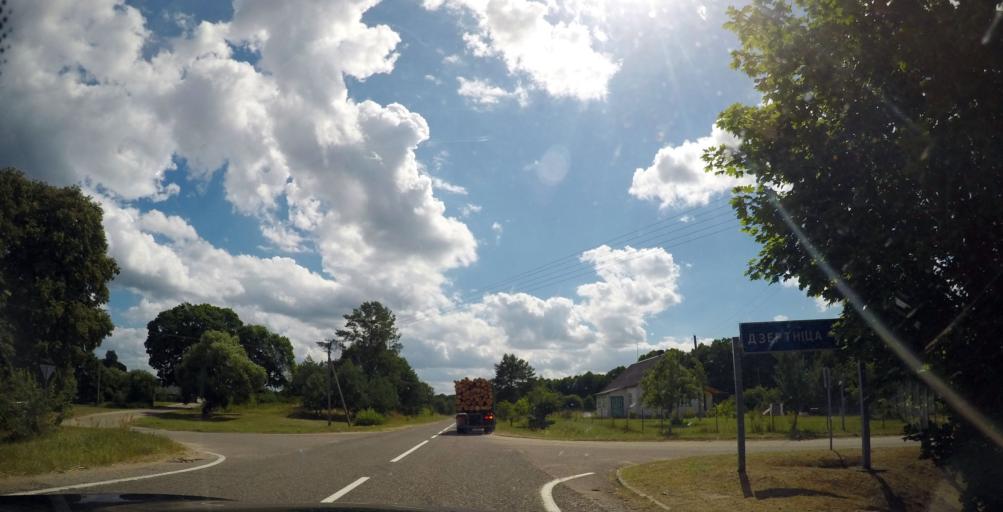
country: BY
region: Grodnenskaya
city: Skidal'
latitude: 53.8233
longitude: 24.2415
